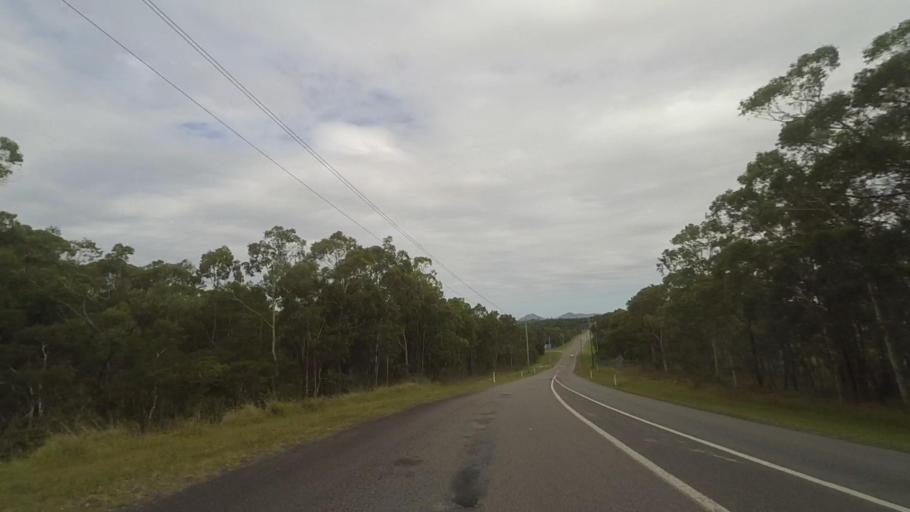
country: AU
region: New South Wales
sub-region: Great Lakes
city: Hawks Nest
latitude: -32.6412
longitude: 152.1452
